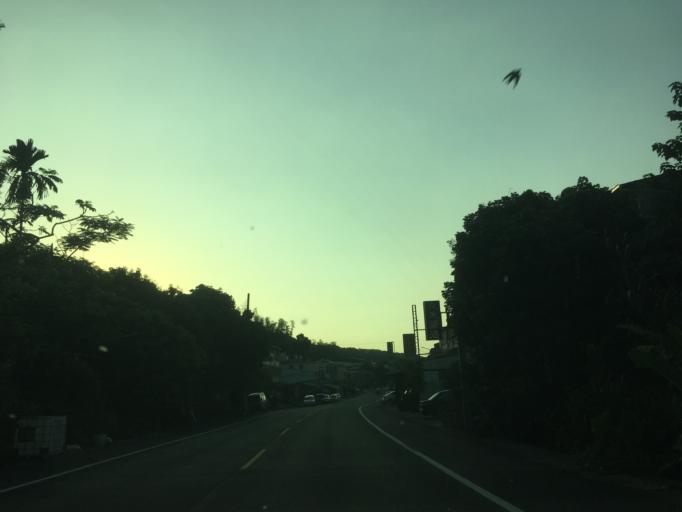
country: TW
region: Taiwan
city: Zhongxing New Village
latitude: 23.9499
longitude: 120.6588
